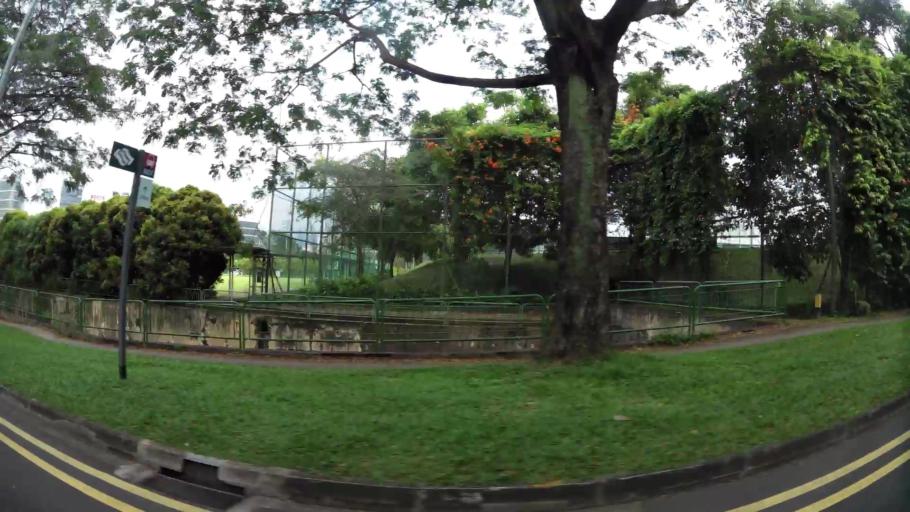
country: SG
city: Singapore
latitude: 1.3462
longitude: 103.8393
